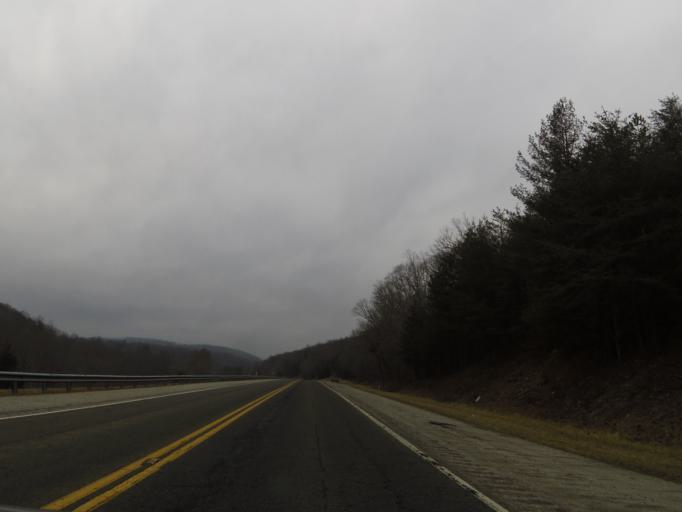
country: US
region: Tennessee
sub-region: Morgan County
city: Wartburg
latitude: 36.1315
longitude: -84.6195
